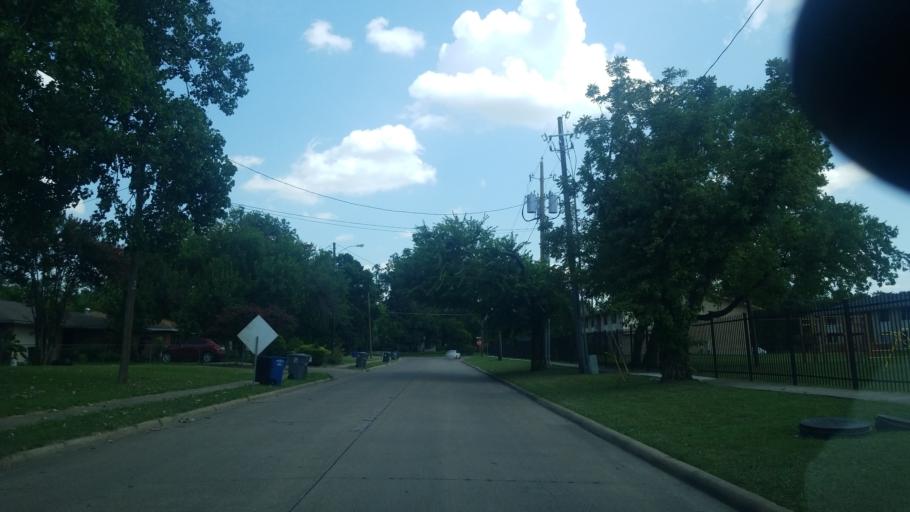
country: US
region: Texas
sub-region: Dallas County
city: Hutchins
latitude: 32.7139
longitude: -96.7618
